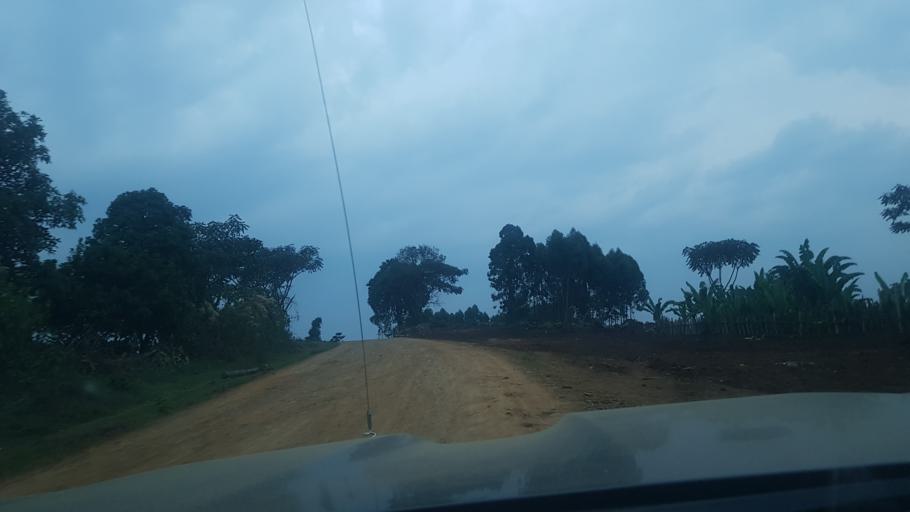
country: ET
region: Oromiya
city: Gore
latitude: 7.7839
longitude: 35.4602
